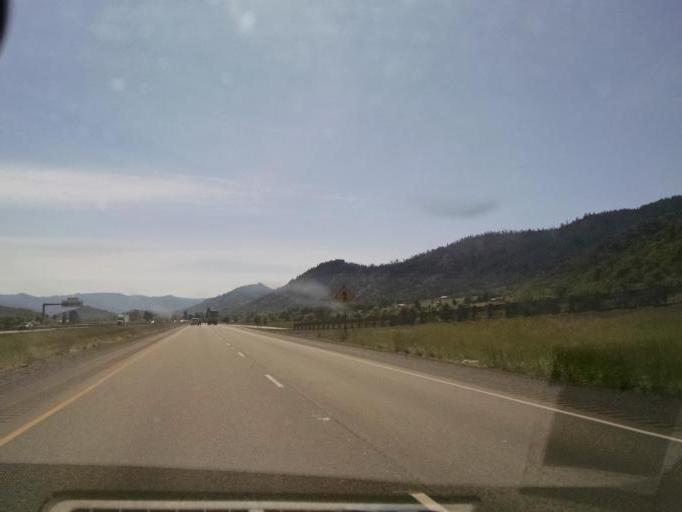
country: US
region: Oregon
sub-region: Douglas County
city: Tri-City
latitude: 43.0057
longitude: -123.3090
